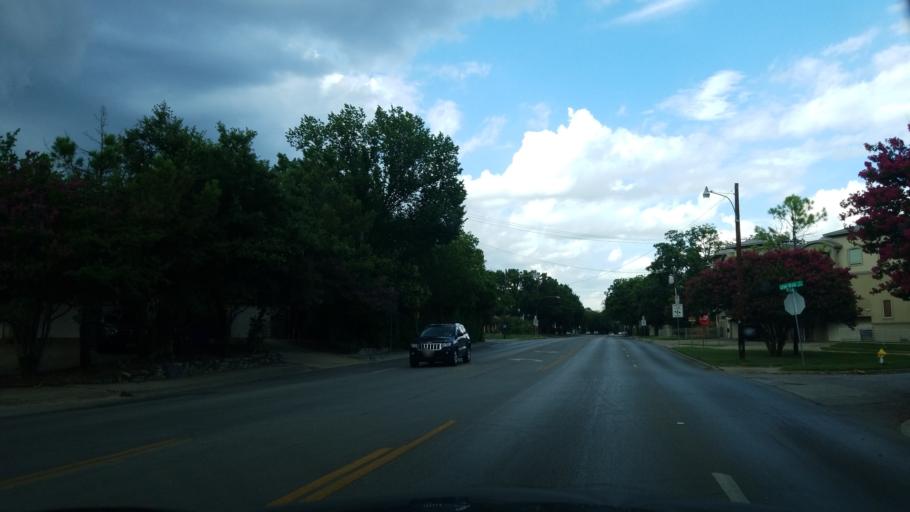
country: US
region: Texas
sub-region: Dallas County
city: Highland Park
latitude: 32.8068
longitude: -96.7675
